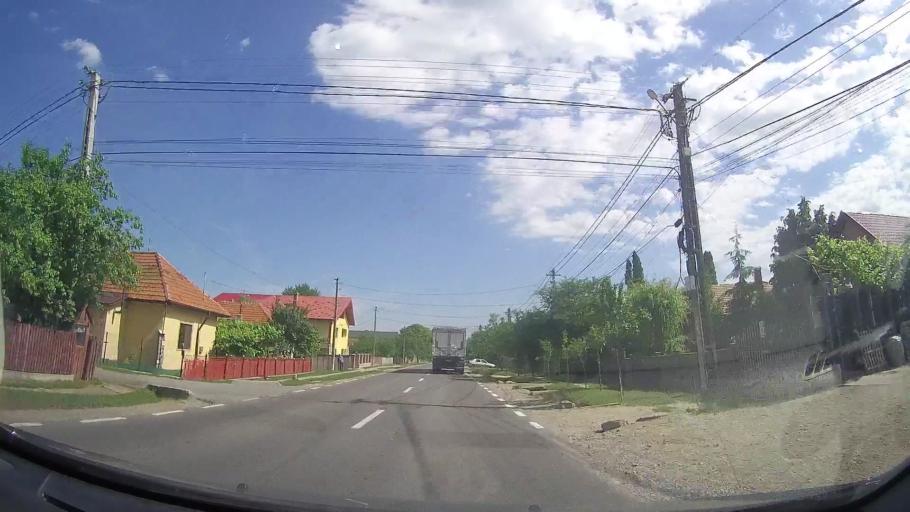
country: RO
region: Prahova
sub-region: Comuna Maneciu-Ungureni
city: Gheaba
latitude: 45.3006
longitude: 25.9981
